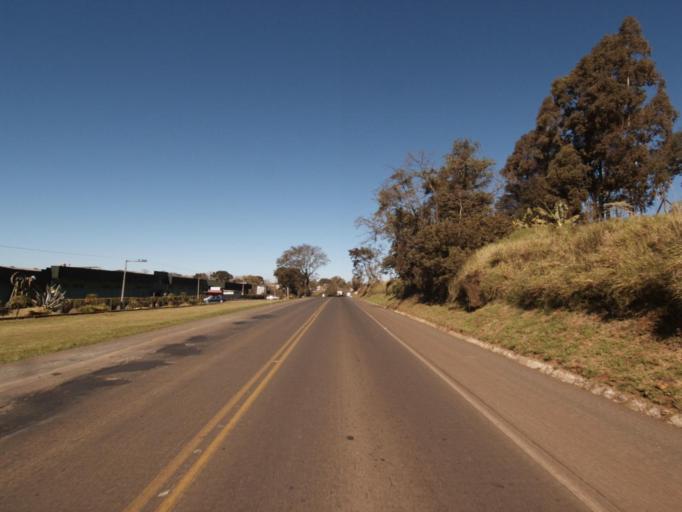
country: BR
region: Santa Catarina
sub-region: Chapeco
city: Chapeco
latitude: -26.8485
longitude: -52.9803
